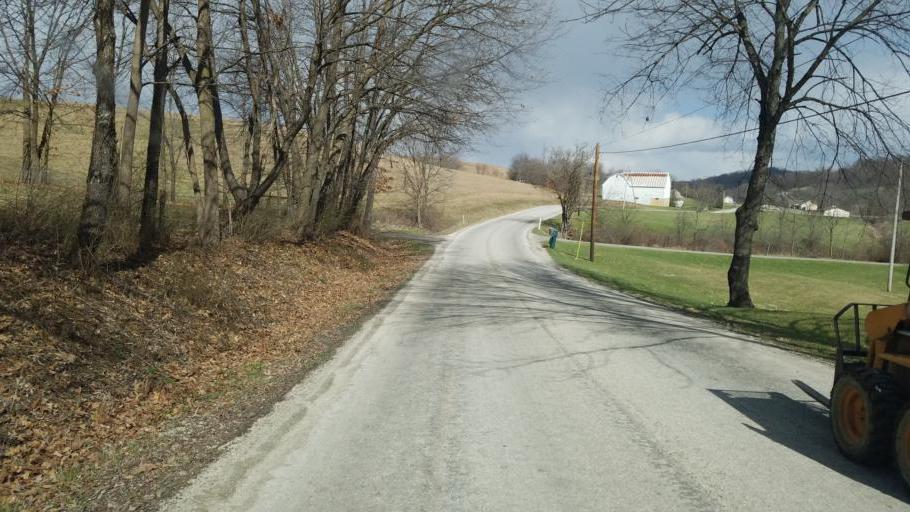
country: US
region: Ohio
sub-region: Tuscarawas County
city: Sugarcreek
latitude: 40.4356
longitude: -81.6839
